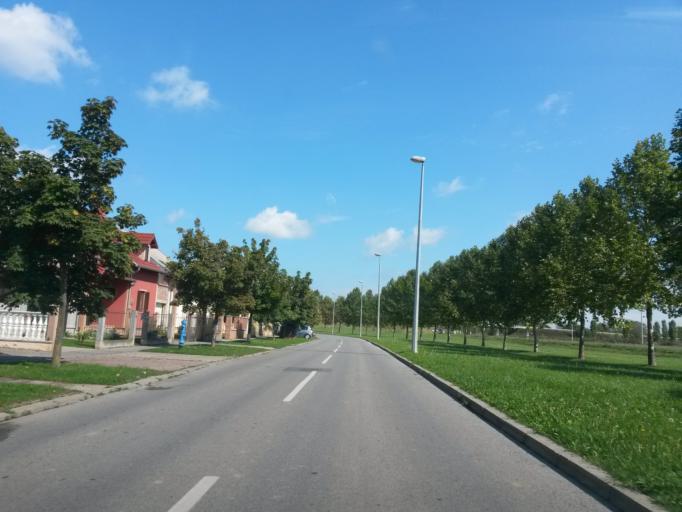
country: HR
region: Osjecko-Baranjska
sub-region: Grad Osijek
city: Osijek
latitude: 45.5411
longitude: 18.7056
